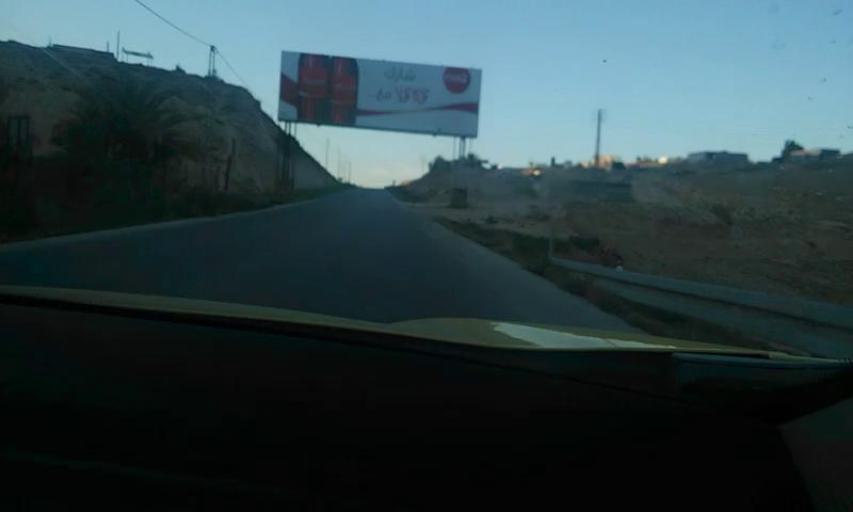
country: PS
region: West Bank
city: An Nuway`imah
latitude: 31.9013
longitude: 35.4266
